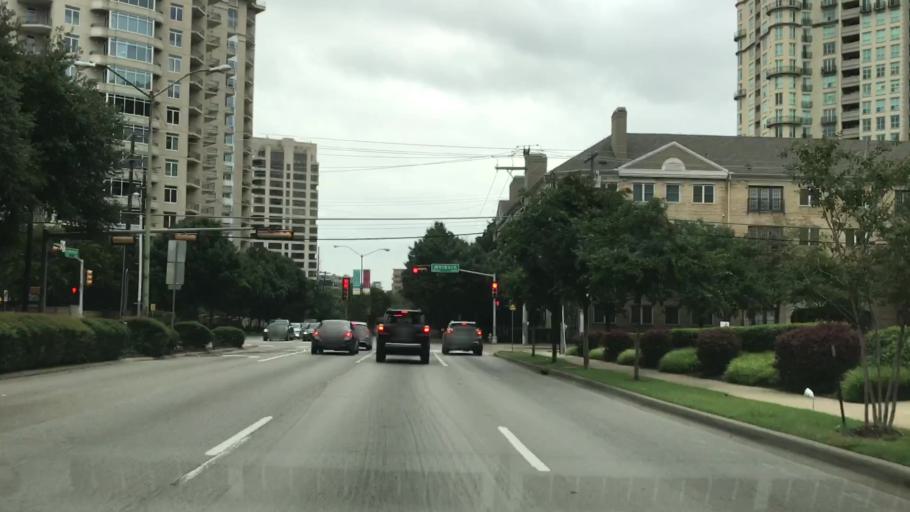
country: US
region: Texas
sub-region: Dallas County
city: Highland Park
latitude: 32.8113
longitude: -96.8050
